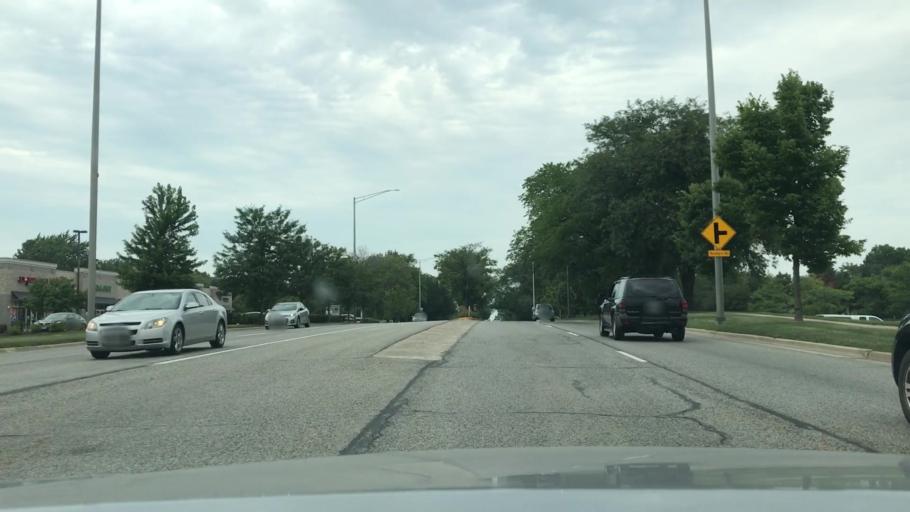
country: US
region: Illinois
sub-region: Will County
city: Bolingbrook
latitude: 41.7043
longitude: -88.0684
